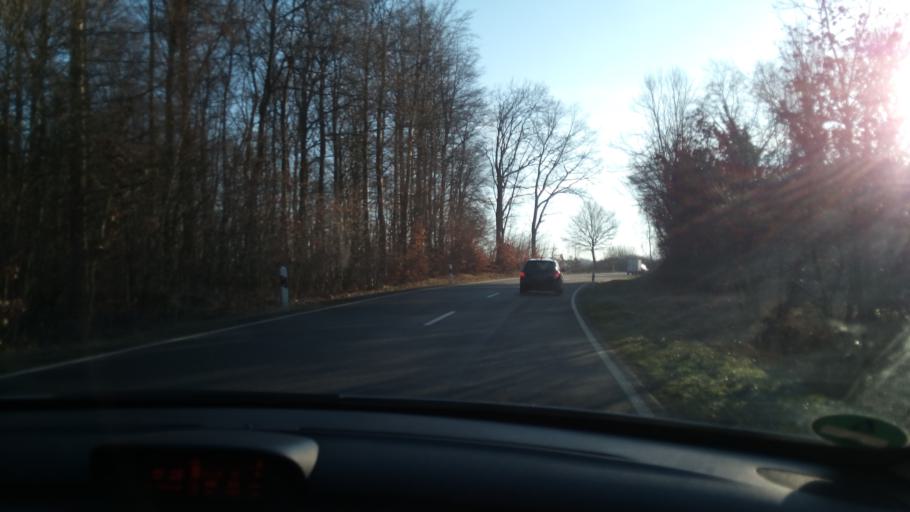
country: DE
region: Schleswig-Holstein
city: Buchhorst
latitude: 53.3904
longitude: 10.5561
